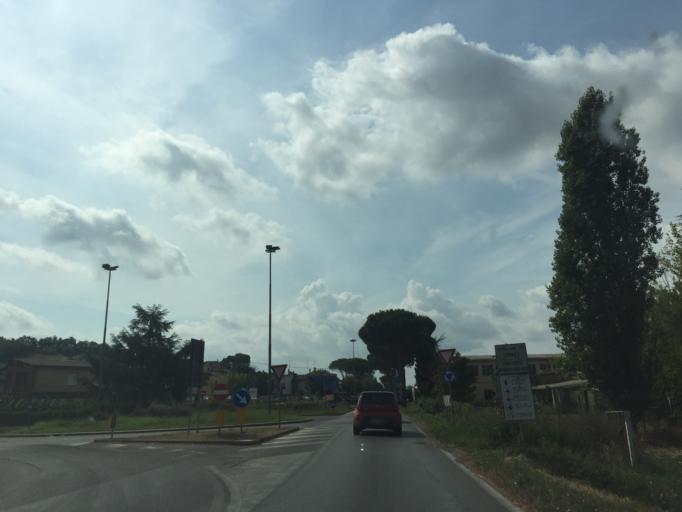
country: IT
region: Tuscany
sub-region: Province of Florence
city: Cerreto Guidi
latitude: 43.7431
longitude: 10.9010
